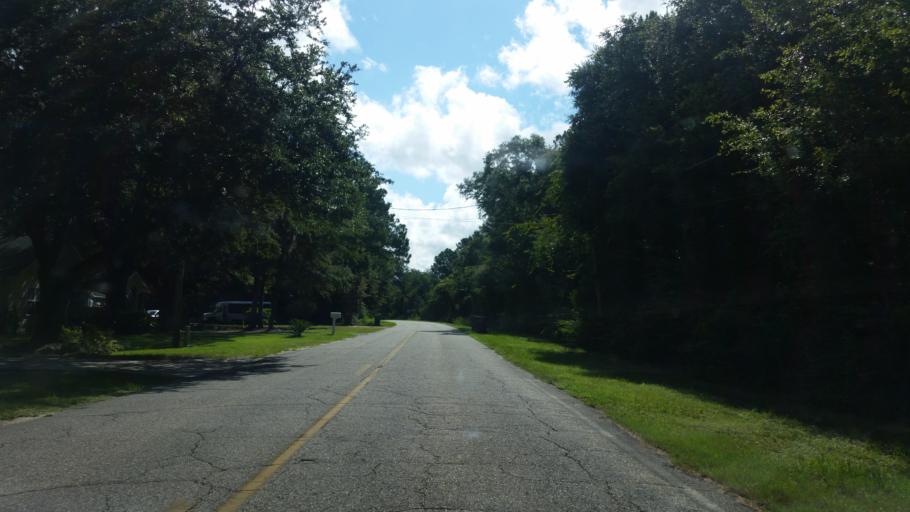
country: US
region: Florida
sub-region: Santa Rosa County
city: Bagdad
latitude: 30.6113
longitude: -87.0495
